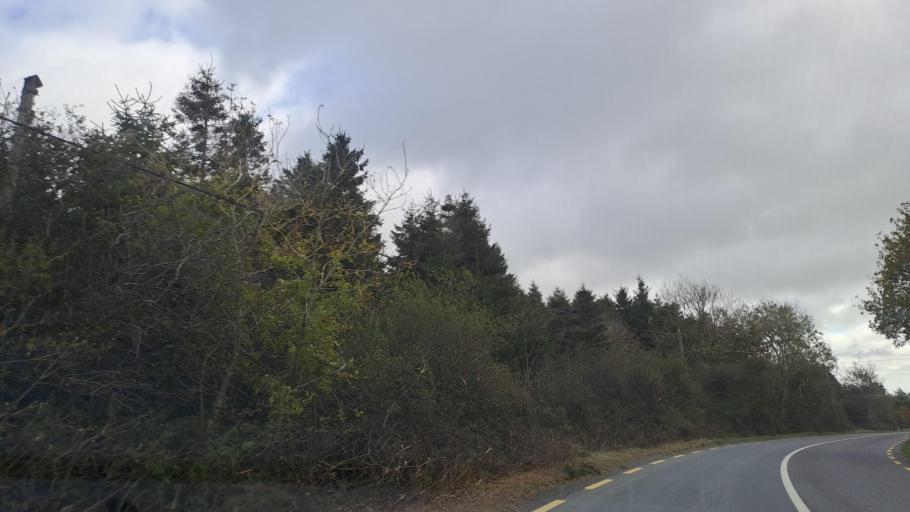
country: IE
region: Ulster
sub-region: An Cabhan
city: Kingscourt
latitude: 53.9285
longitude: -6.8784
